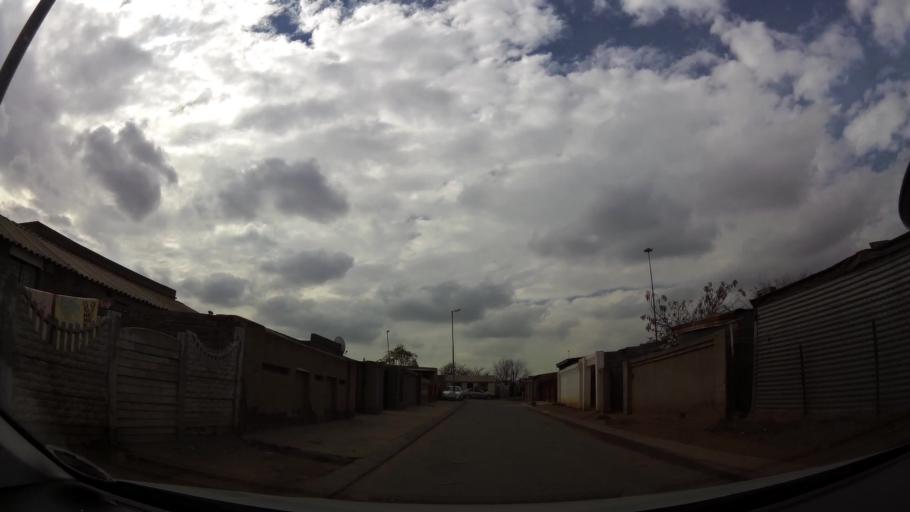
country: ZA
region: Gauteng
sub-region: City of Johannesburg Metropolitan Municipality
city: Soweto
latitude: -26.2711
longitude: 27.8539
